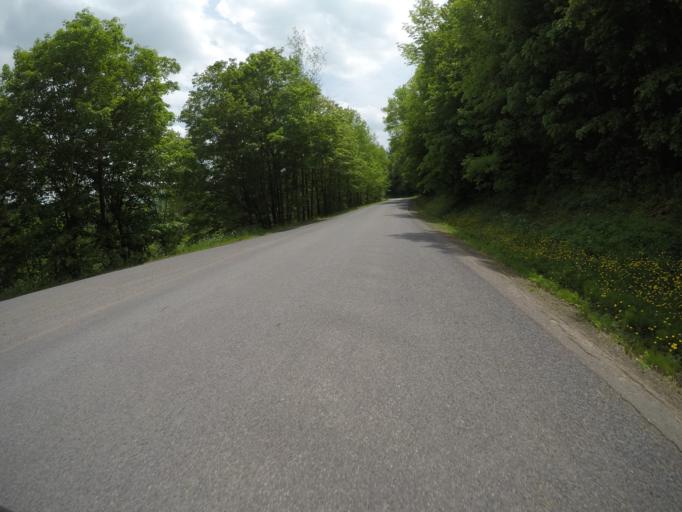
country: US
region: New York
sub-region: Delaware County
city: Stamford
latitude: 42.2359
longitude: -74.6965
